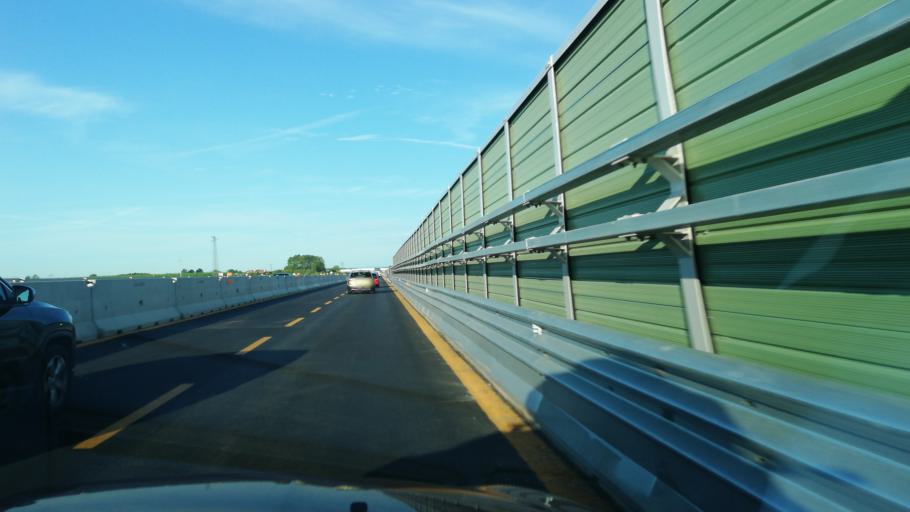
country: IT
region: Friuli Venezia Giulia
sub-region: Provincia di Udine
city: Porpetto
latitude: 45.8594
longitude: 13.1928
